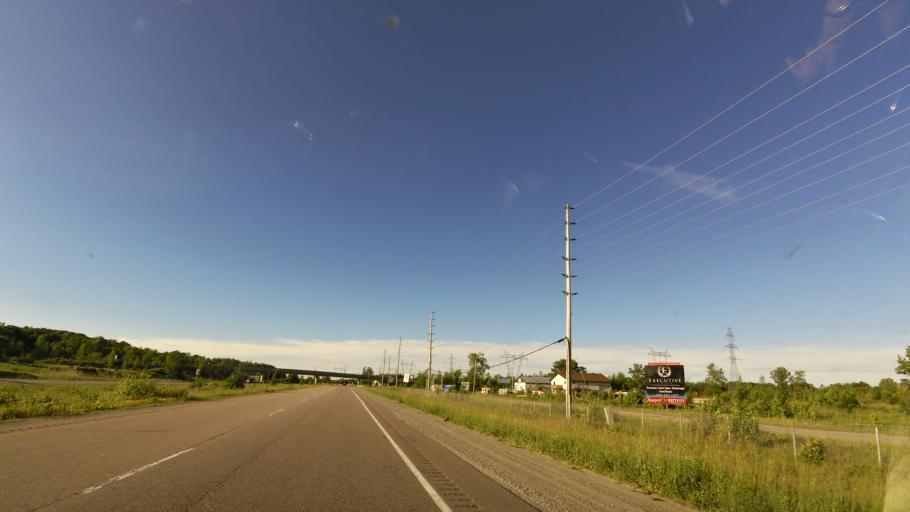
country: CA
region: Ontario
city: Midland
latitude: 44.7643
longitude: -79.6954
